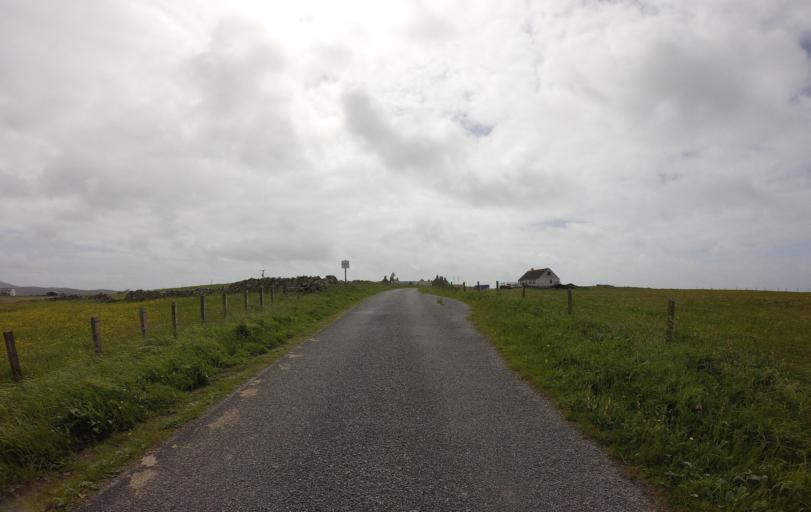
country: GB
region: Scotland
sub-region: Eilean Siar
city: Isle of South Uist
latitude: 57.2623
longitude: -7.4065
